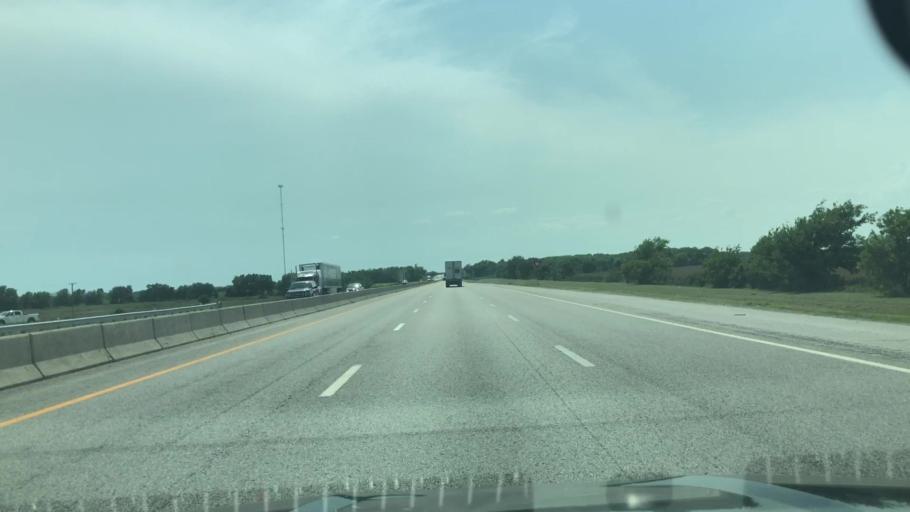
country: US
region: Oklahoma
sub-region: Ottawa County
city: Afton
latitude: 36.7223
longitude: -94.9358
